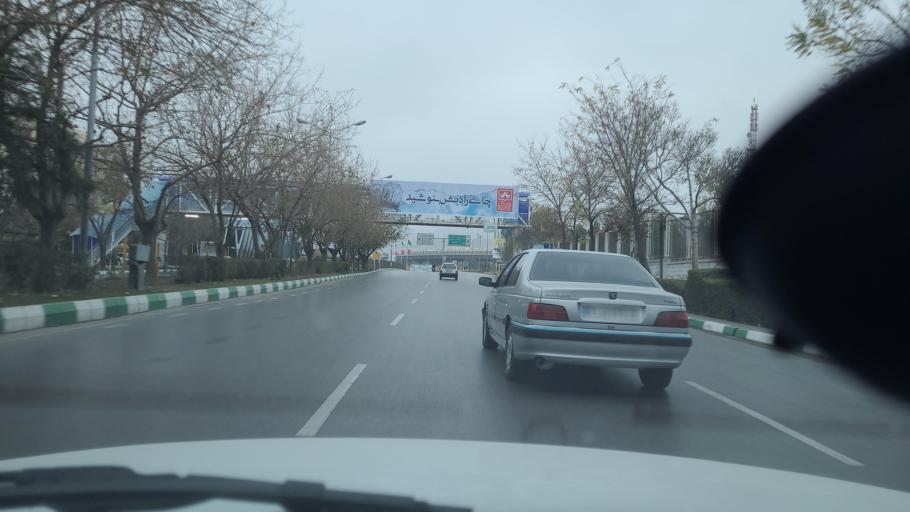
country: IR
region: Razavi Khorasan
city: Mashhad
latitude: 36.2898
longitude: 59.5582
